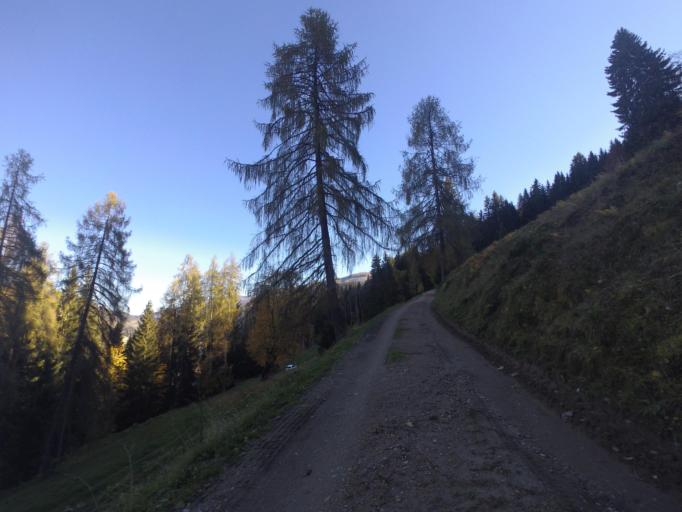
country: AT
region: Salzburg
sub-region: Politischer Bezirk Sankt Johann im Pongau
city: Sankt Johann im Pongau
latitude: 47.3297
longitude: 13.2172
